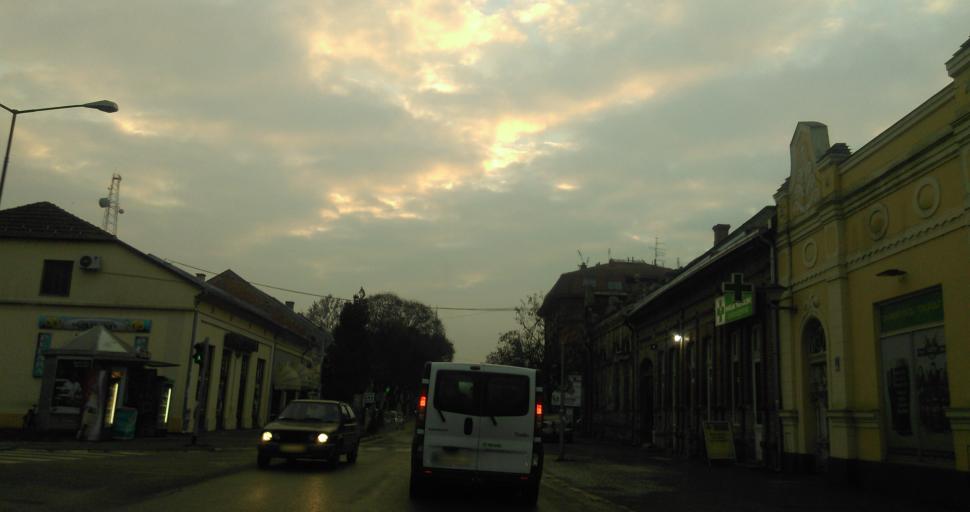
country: RS
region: Autonomna Pokrajina Vojvodina
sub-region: Juznobacki Okrug
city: Becej
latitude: 45.6178
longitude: 20.0450
